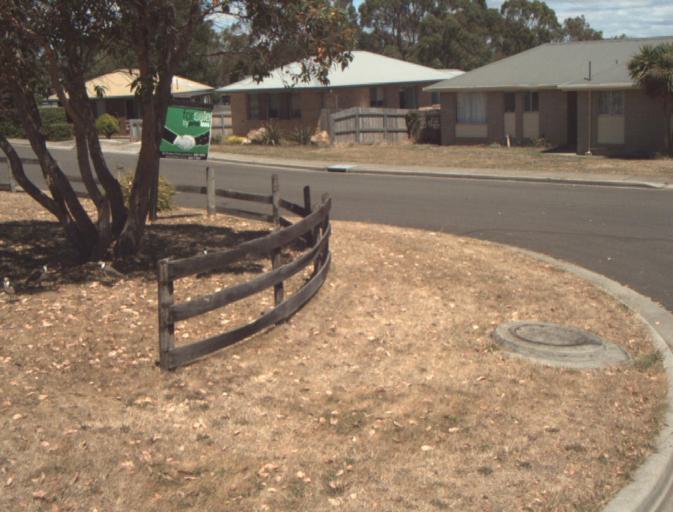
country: AU
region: Tasmania
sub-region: Launceston
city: Mayfield
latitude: -41.3776
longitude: 147.1375
